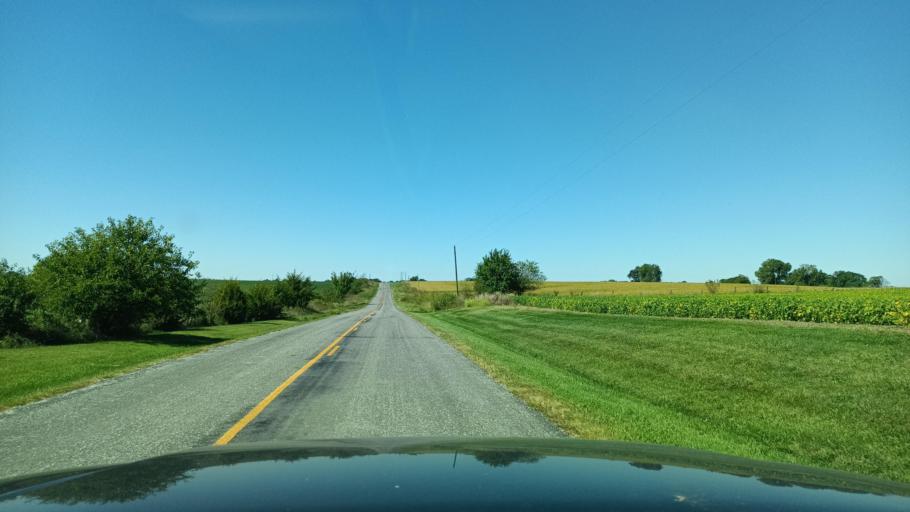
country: US
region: Missouri
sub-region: Adair County
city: Kirksville
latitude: 40.3304
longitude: -92.5241
